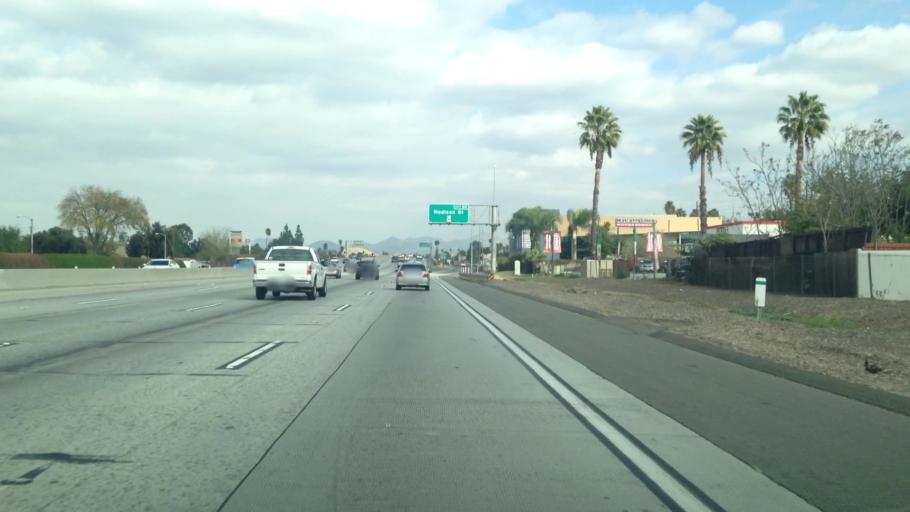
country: US
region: California
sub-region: Riverside County
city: Riverside
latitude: 33.9334
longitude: -117.4090
